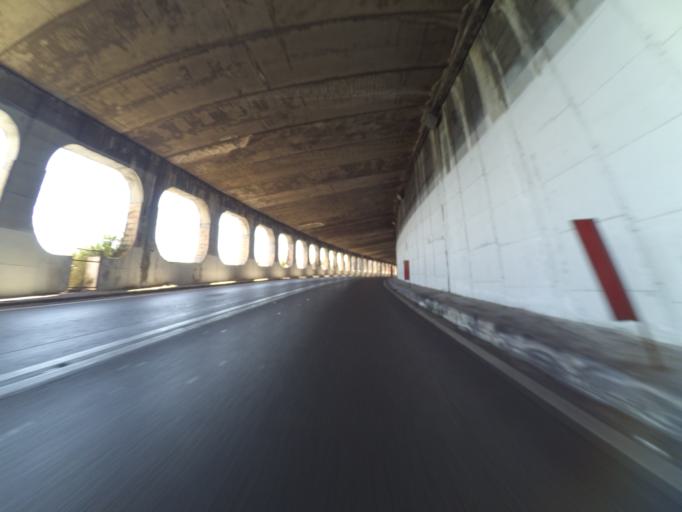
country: IT
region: Latium
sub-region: Provincia di Latina
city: Sperlonga
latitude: 41.2381
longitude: 13.4815
